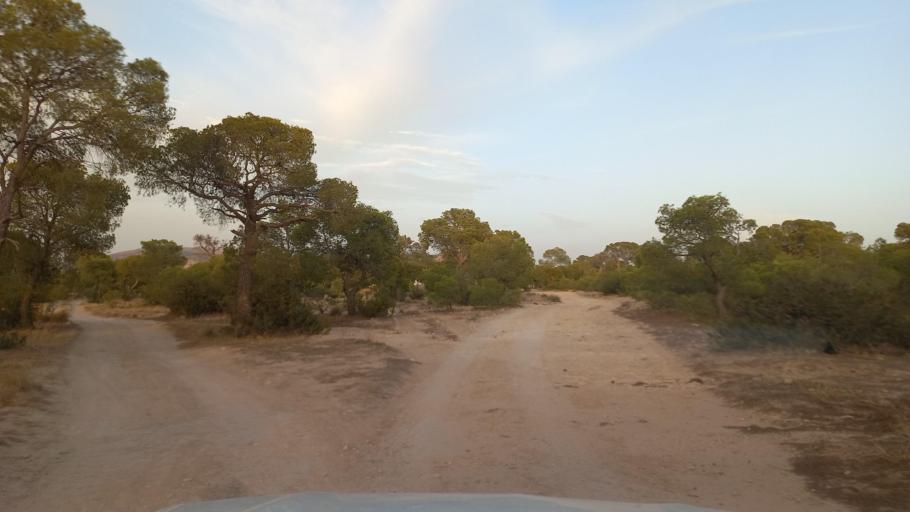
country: TN
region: Al Qasrayn
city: Sbiba
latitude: 35.4250
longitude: 8.9177
